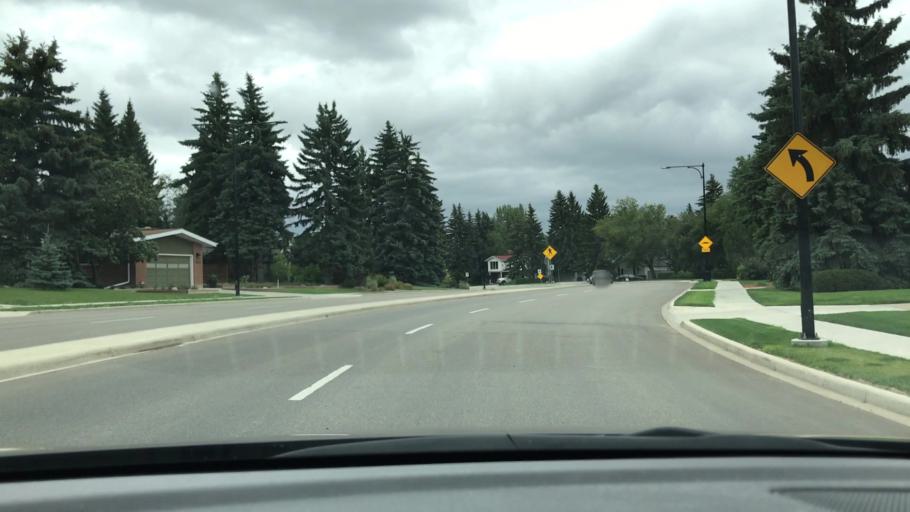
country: CA
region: Alberta
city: Edmonton
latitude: 53.5187
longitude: -113.5596
